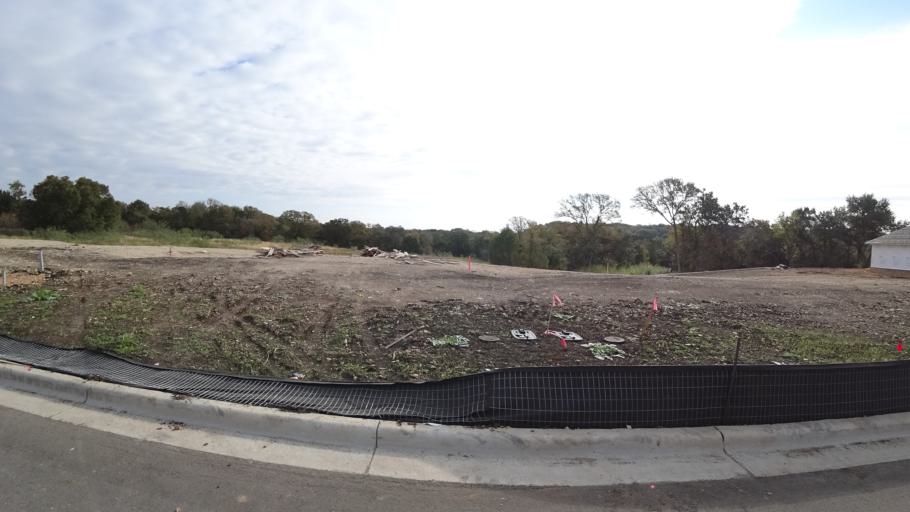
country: US
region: Texas
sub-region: Travis County
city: Manchaca
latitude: 30.1308
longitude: -97.8438
